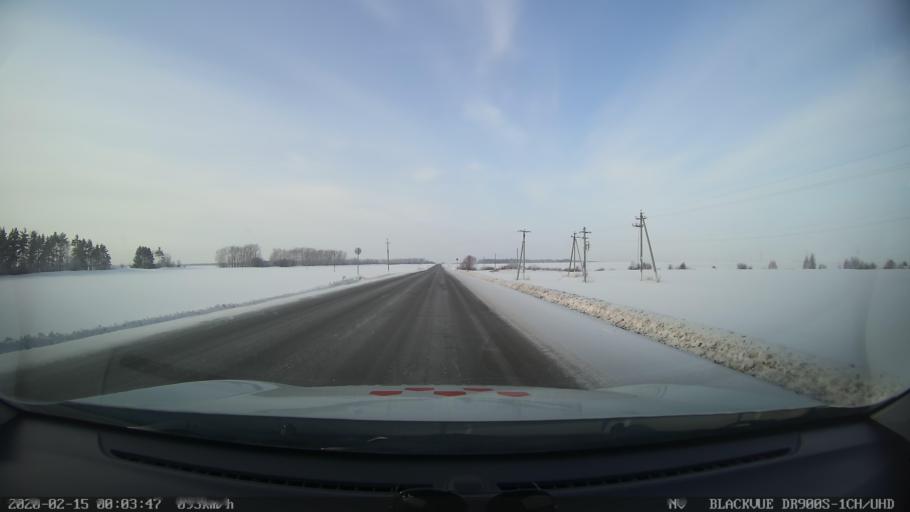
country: RU
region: Tatarstan
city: Kuybyshevskiy Zaton
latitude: 55.3757
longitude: 48.9927
